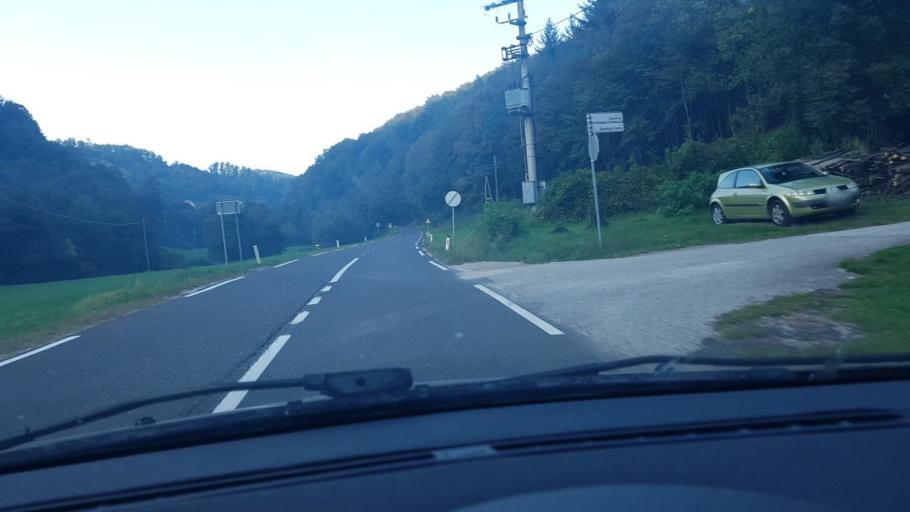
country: SI
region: Majsperk
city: Majsperk
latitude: 46.3156
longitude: 15.7184
